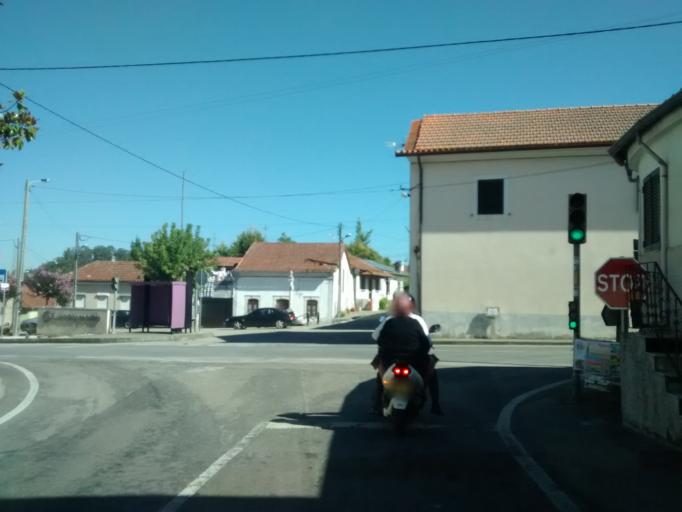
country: PT
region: Aveiro
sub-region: Anadia
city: Sangalhos
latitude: 40.4380
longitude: -8.4981
